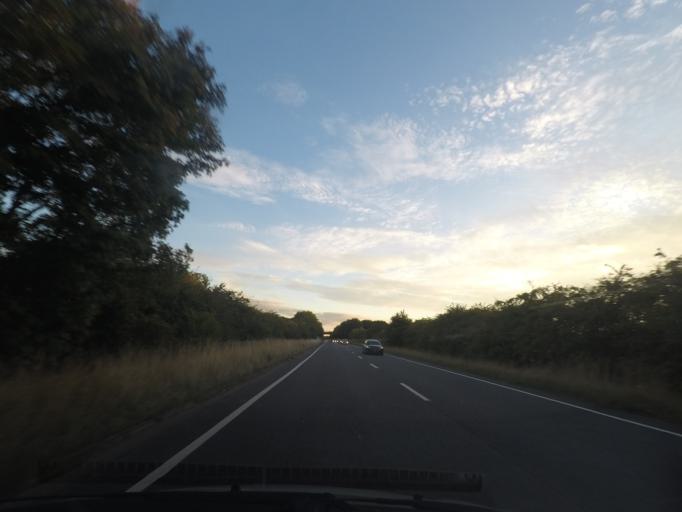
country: GB
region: England
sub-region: Oxfordshire
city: Shrivenham
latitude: 51.6051
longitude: -1.6618
